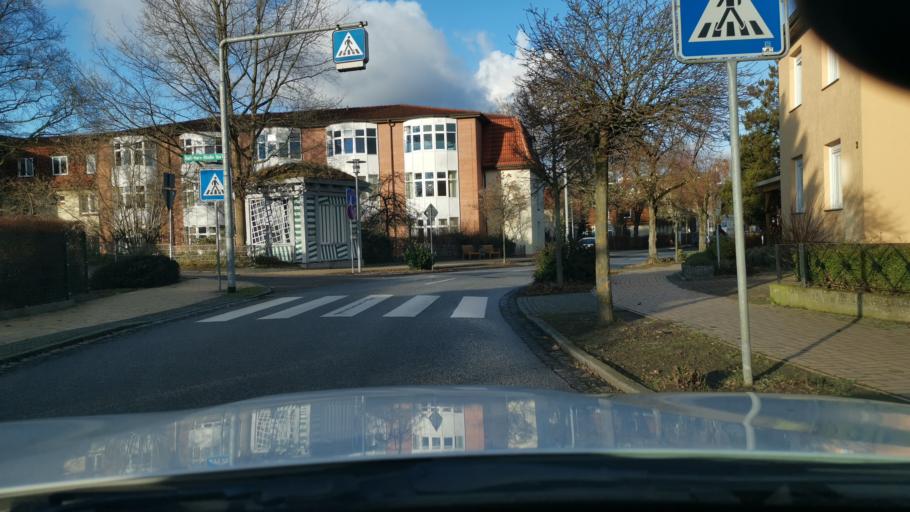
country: DE
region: Mecklenburg-Vorpommern
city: Tessin
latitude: 54.0263
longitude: 12.4613
